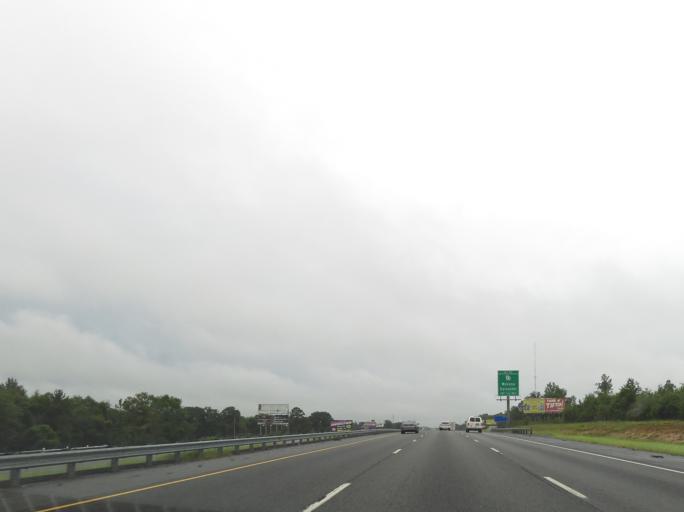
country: US
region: Georgia
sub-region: Crisp County
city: Cordele
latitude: 31.9176
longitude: -83.7422
